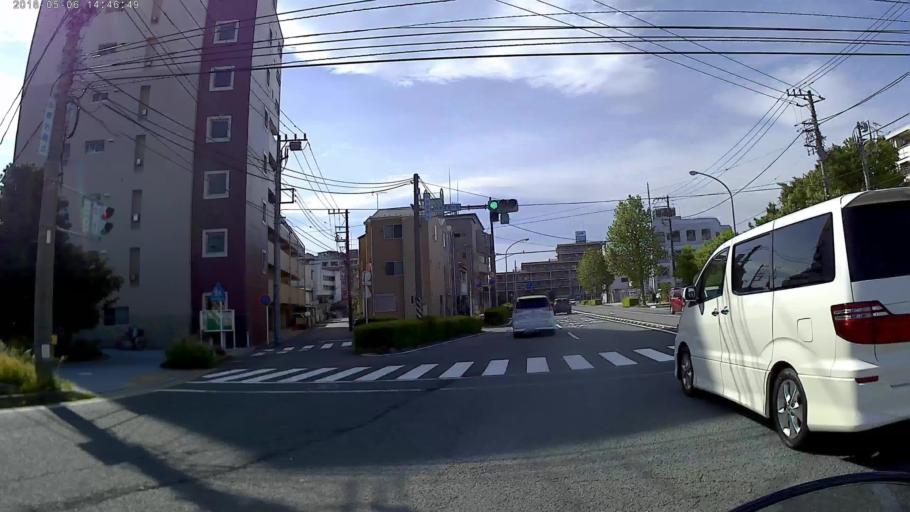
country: JP
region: Kanagawa
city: Yokohama
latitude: 35.4116
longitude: 139.6255
